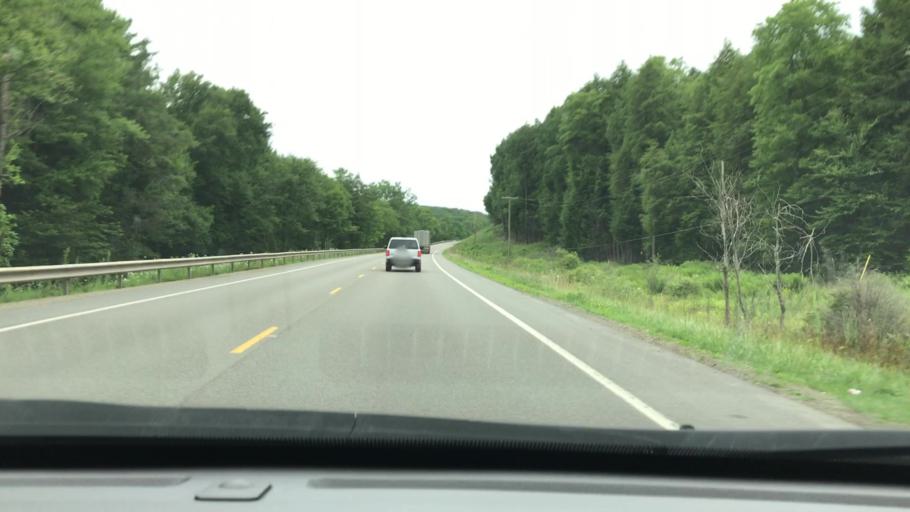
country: US
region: Pennsylvania
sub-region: McKean County
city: Kane
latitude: 41.6851
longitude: -78.6888
